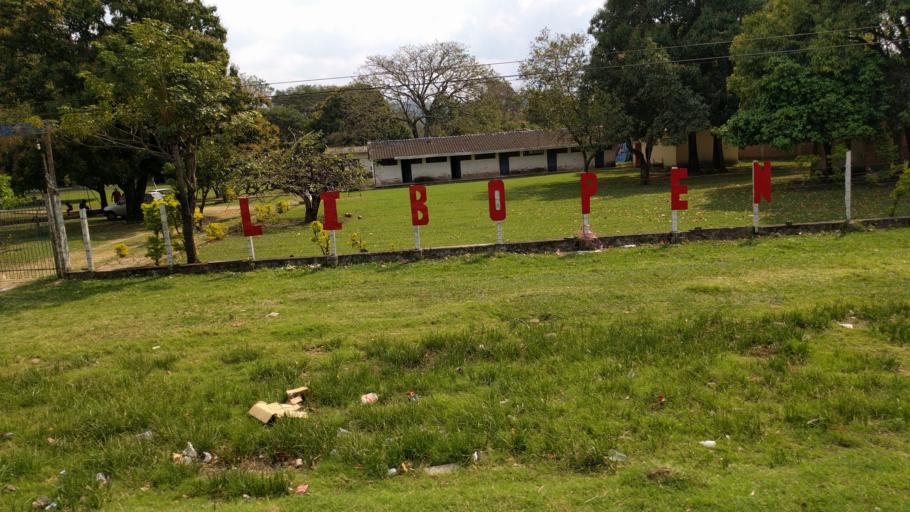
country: BO
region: Santa Cruz
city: Limoncito
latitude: -18.0149
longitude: -63.3953
